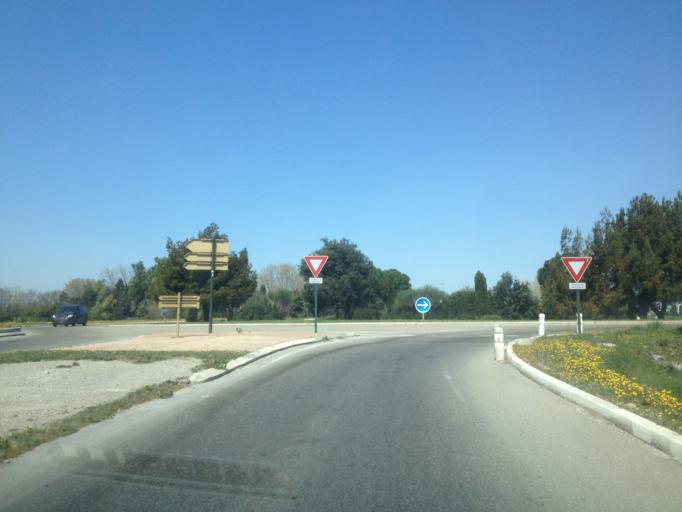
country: FR
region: Provence-Alpes-Cote d'Azur
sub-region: Departement du Vaucluse
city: Vedene
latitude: 43.9771
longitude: 4.8875
